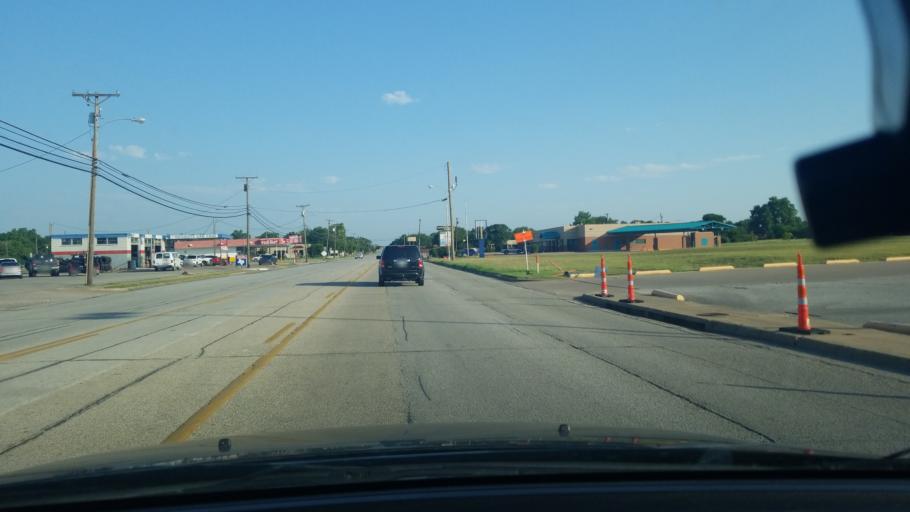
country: US
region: Texas
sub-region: Dallas County
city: Mesquite
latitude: 32.8030
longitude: -96.6466
